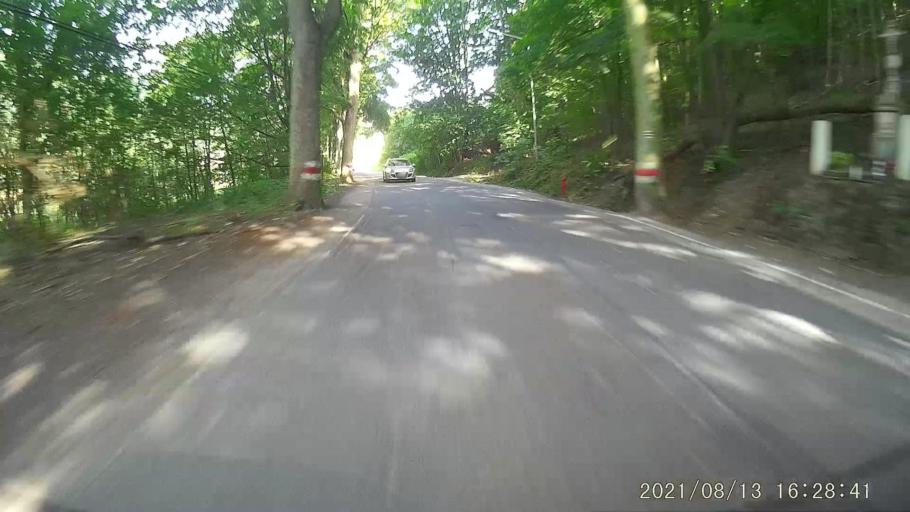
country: PL
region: Lower Silesian Voivodeship
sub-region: Powiat klodzki
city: Kudowa-Zdroj
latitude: 50.4454
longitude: 16.2590
